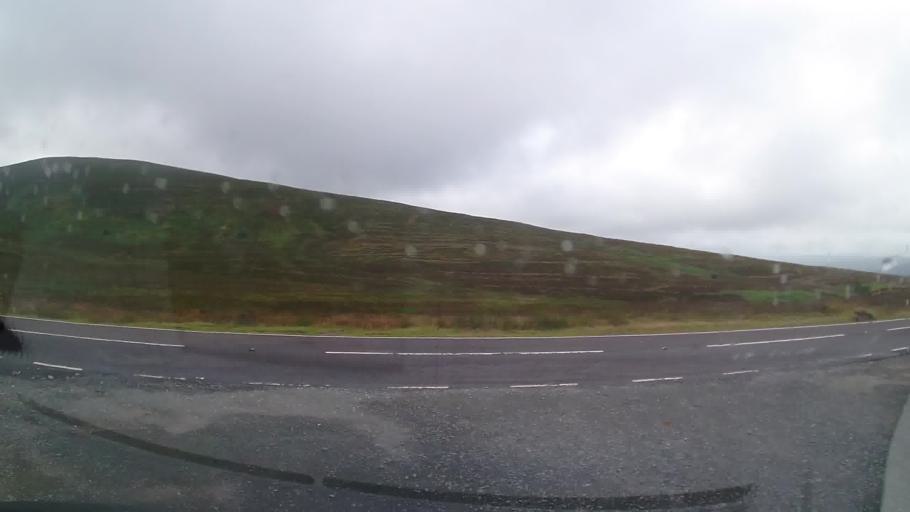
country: GB
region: Wales
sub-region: Denbighshire
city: Llandrillo
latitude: 52.8807
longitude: -3.4796
